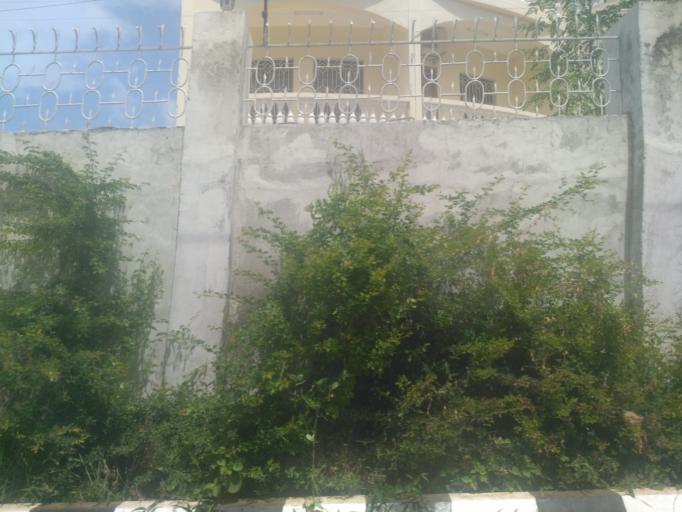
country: TZ
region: Zanzibar Urban/West
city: Zanzibar
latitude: -6.2143
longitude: 39.2066
